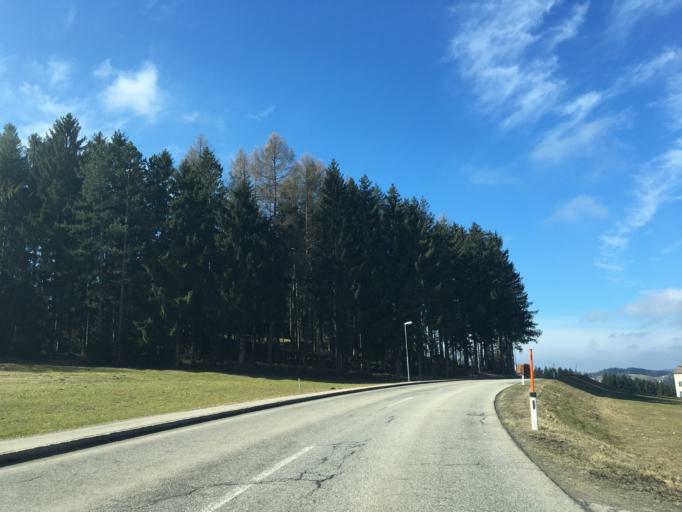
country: AT
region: Upper Austria
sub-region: Politischer Bezirk Perg
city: Sankt Georgen am Walde
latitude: 48.3625
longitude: 14.9070
